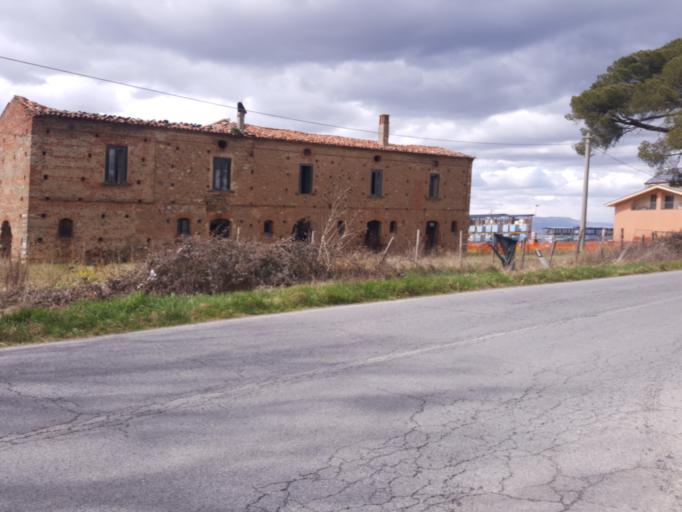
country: IT
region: Calabria
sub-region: Provincia di Cosenza
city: Piane Crati
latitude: 39.2194
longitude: 16.3062
